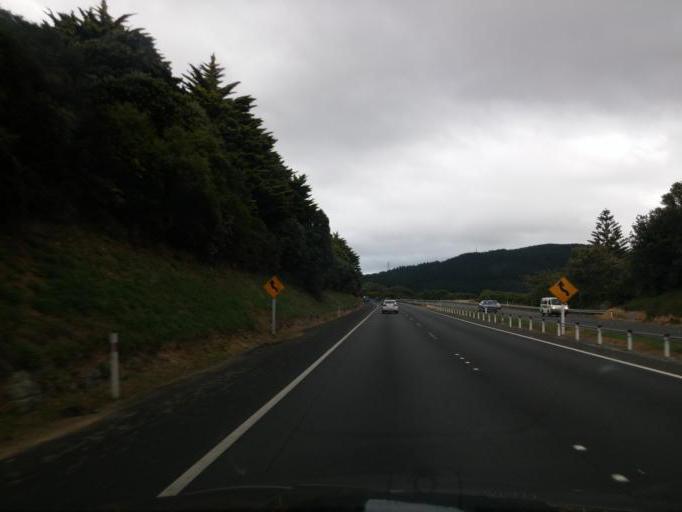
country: NZ
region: Wellington
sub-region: Porirua City
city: Porirua
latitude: -41.1780
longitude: 174.8296
